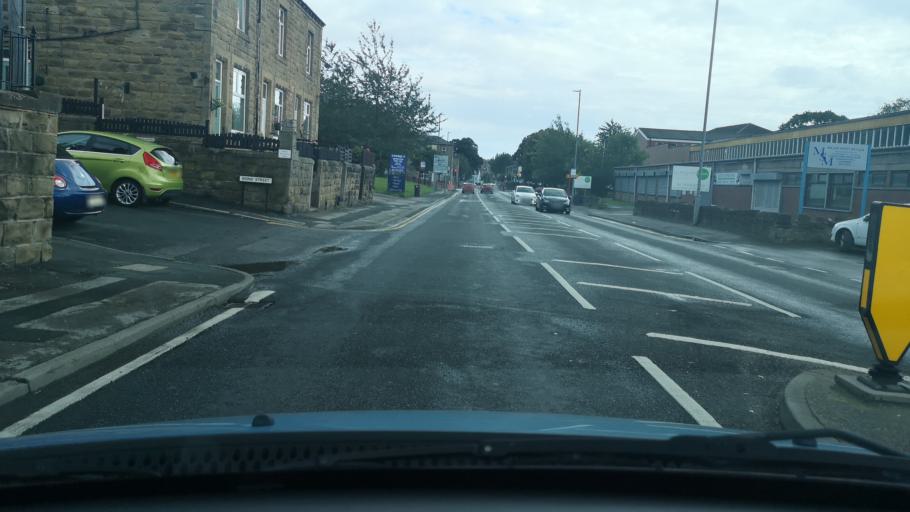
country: GB
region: England
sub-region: Kirklees
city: Batley
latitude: 53.7177
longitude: -1.6368
